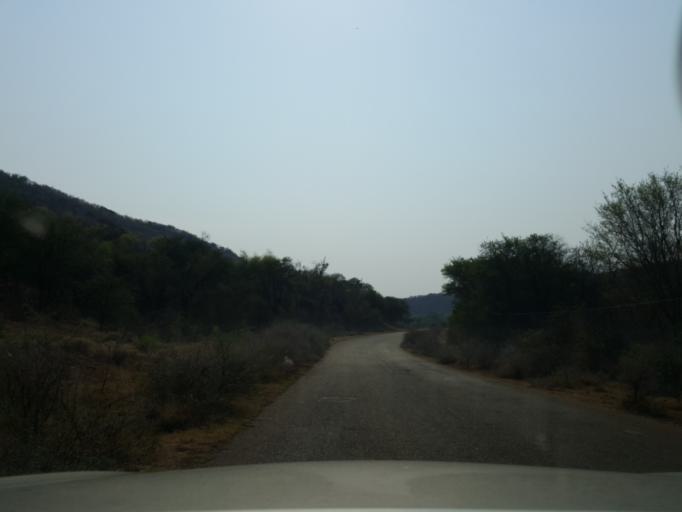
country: BW
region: South East
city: Lobatse
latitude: -25.3292
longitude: 25.7823
